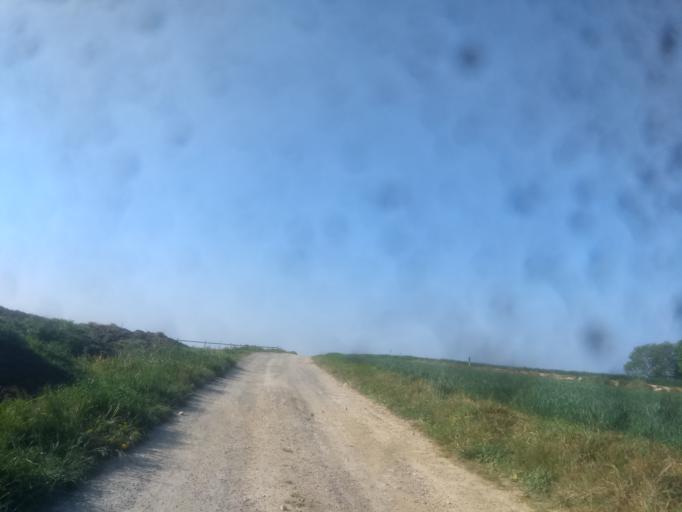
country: FR
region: Nord-Pas-de-Calais
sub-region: Departement du Pas-de-Calais
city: Beaurains
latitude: 50.2642
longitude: 2.8062
